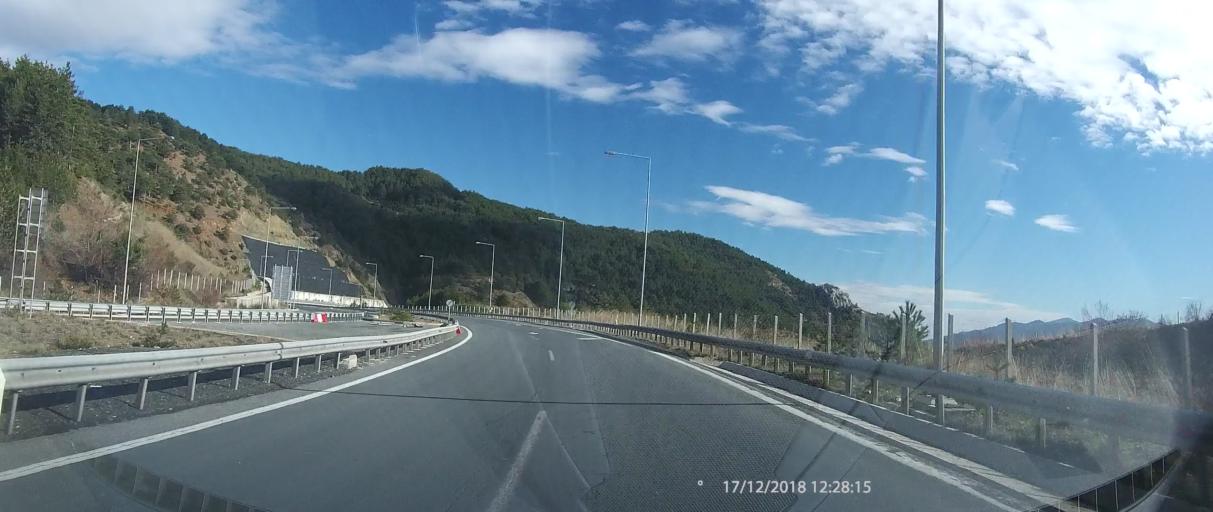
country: GR
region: Epirus
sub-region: Nomos Ioanninon
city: Metsovo
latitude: 39.7890
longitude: 21.2726
